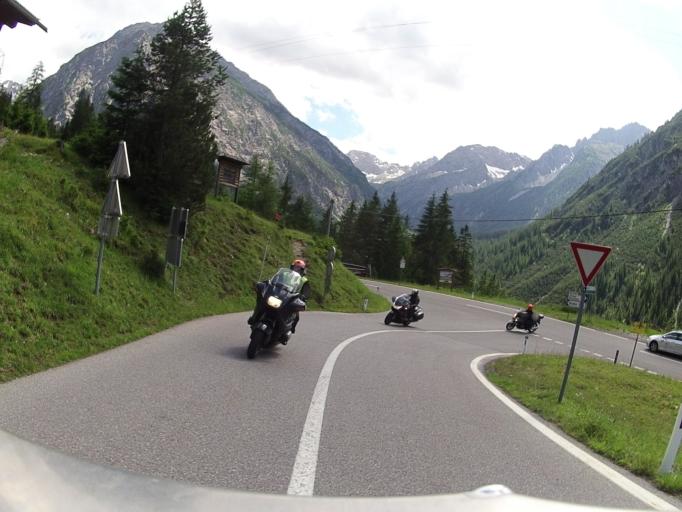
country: AT
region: Tyrol
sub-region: Politischer Bezirk Reutte
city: Gramais
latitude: 47.2891
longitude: 10.6053
